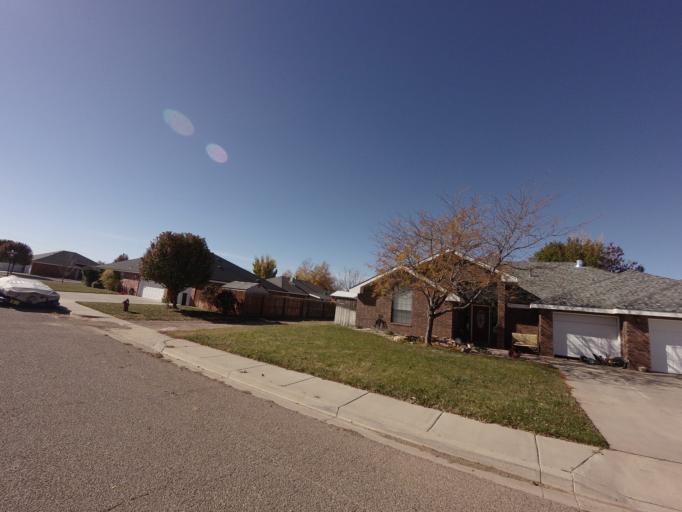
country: US
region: New Mexico
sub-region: Curry County
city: Clovis
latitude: 34.4135
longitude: -103.1675
